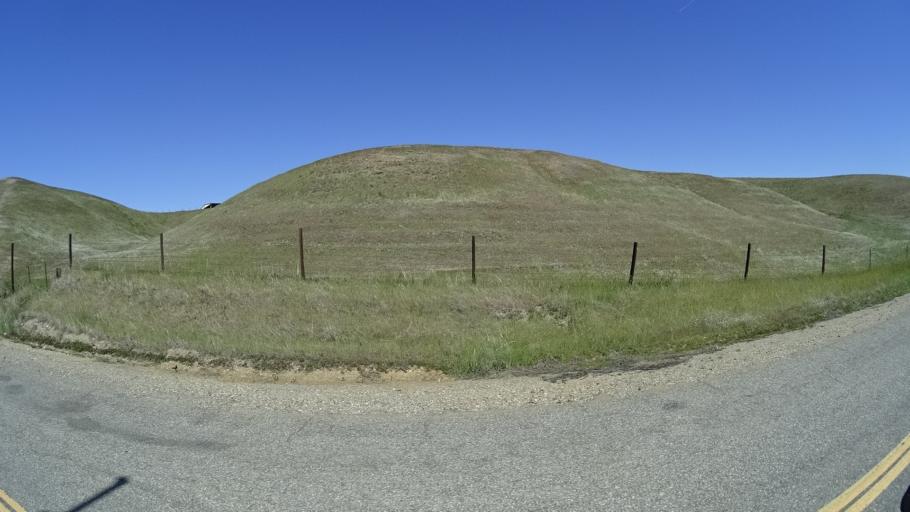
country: US
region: California
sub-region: Glenn County
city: Orland
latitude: 39.7804
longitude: -122.3052
